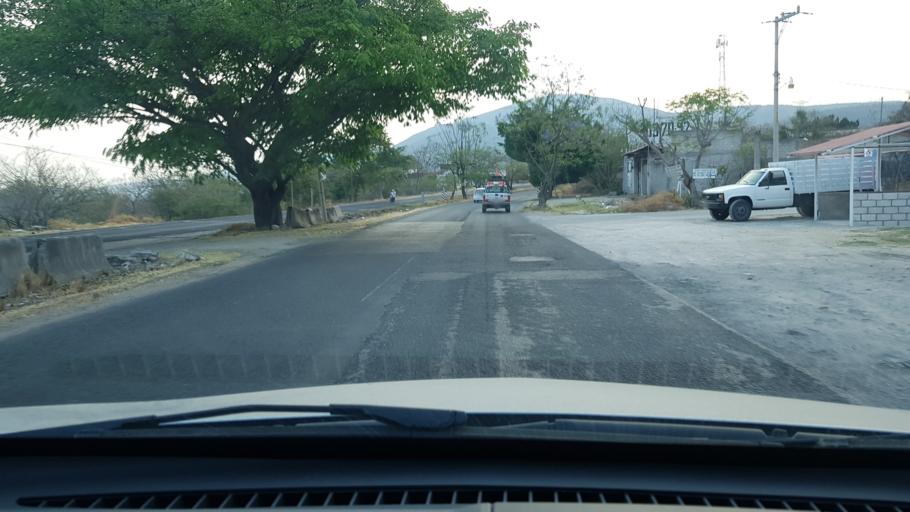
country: MX
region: Morelos
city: Yautepec
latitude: 18.8650
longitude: -99.0915
